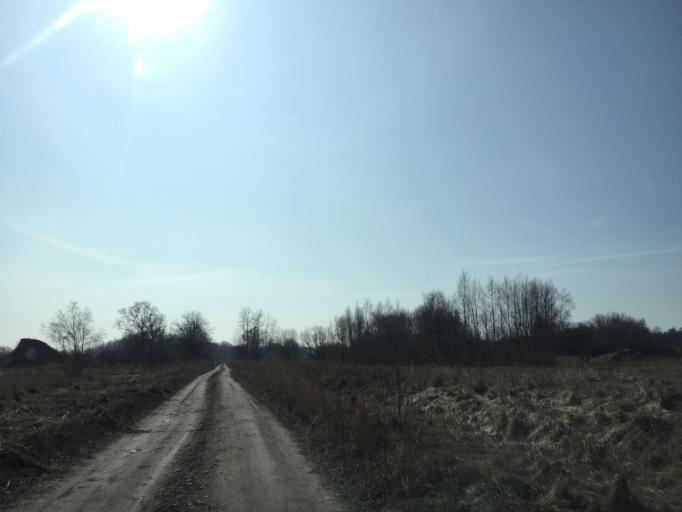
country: LV
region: Dundaga
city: Dundaga
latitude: 57.9290
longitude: 22.0630
